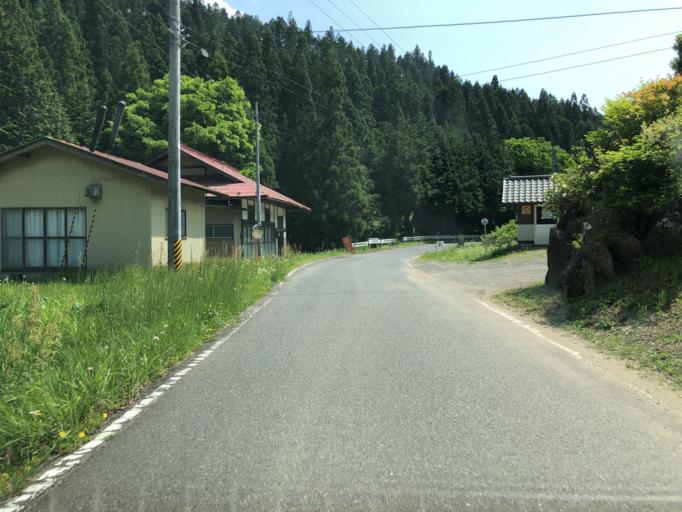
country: JP
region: Fukushima
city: Ishikawa
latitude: 37.0401
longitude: 140.5697
